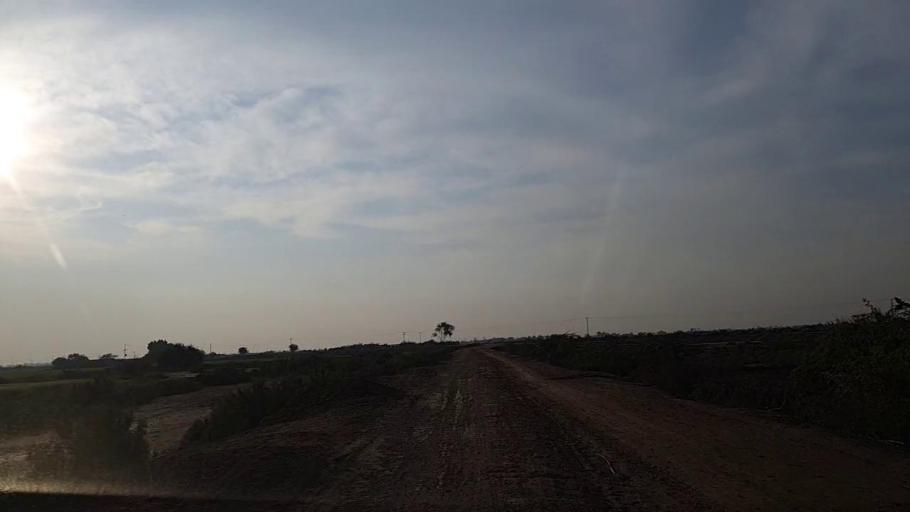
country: PK
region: Sindh
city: Bandhi
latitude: 26.5650
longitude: 68.2492
